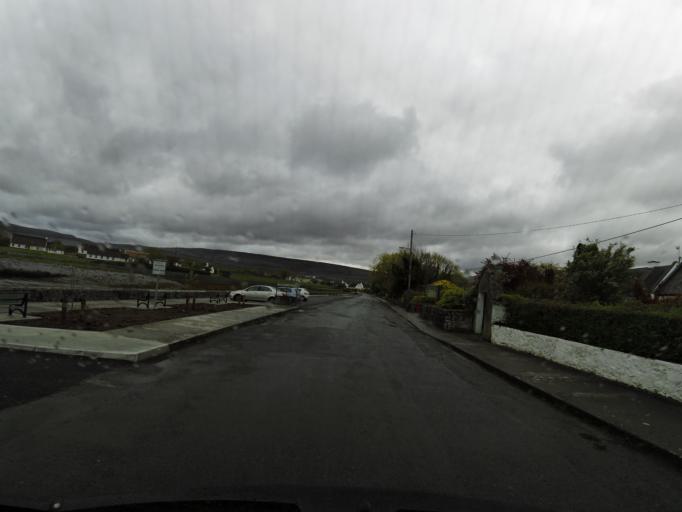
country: IE
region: Connaught
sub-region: County Galway
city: Bearna
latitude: 53.1192
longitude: -9.1534
